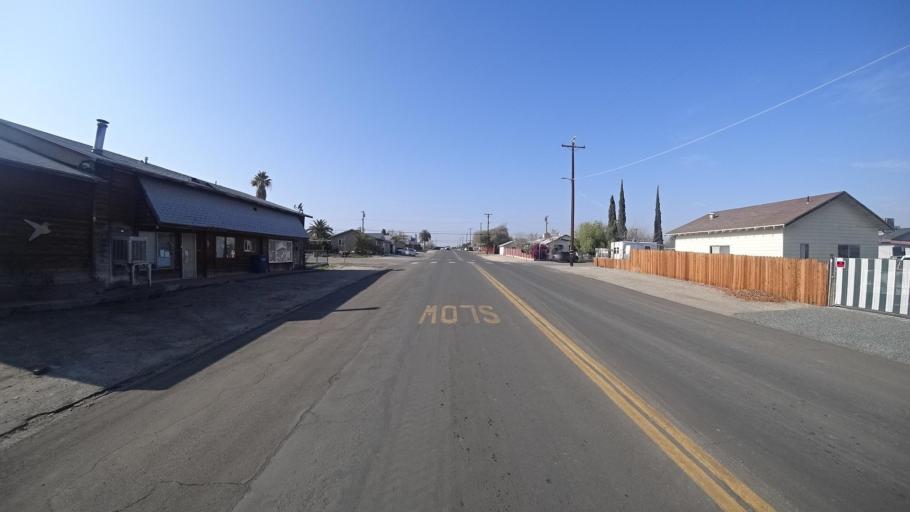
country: US
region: California
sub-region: Kern County
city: Ford City
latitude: 35.1545
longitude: -119.4609
